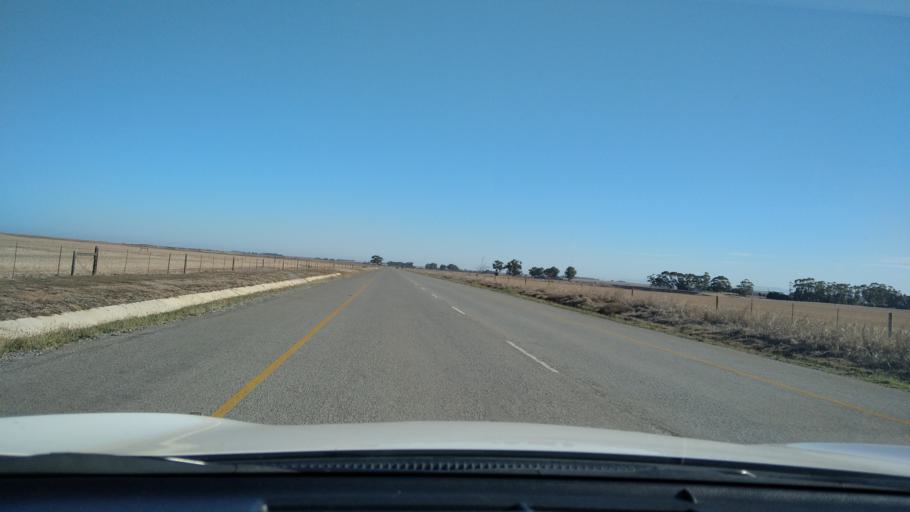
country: ZA
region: Western Cape
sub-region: West Coast District Municipality
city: Moorreesburg
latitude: -33.2919
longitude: 18.6092
